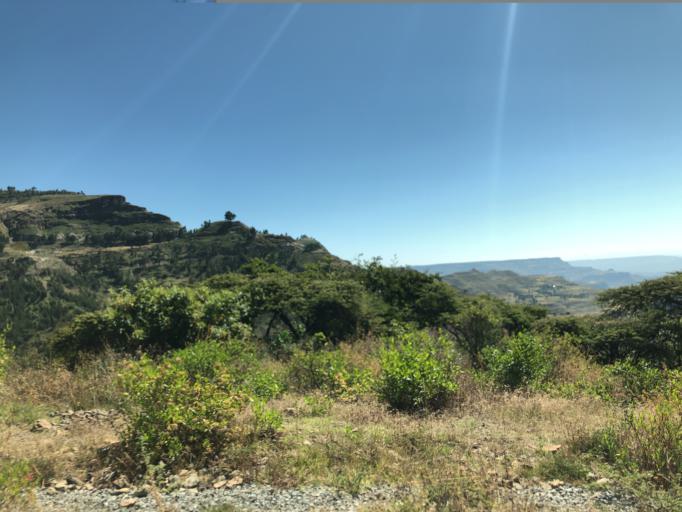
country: ET
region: Amhara
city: Lalibela
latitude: 11.8062
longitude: 38.5706
